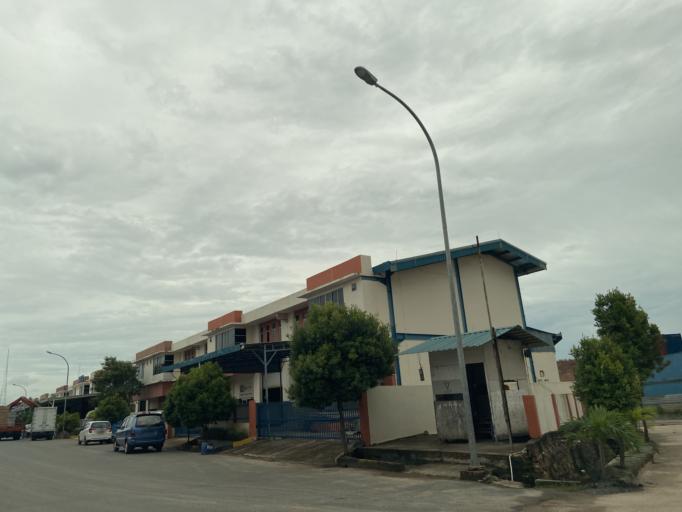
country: SG
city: Singapore
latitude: 1.1654
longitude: 104.0196
